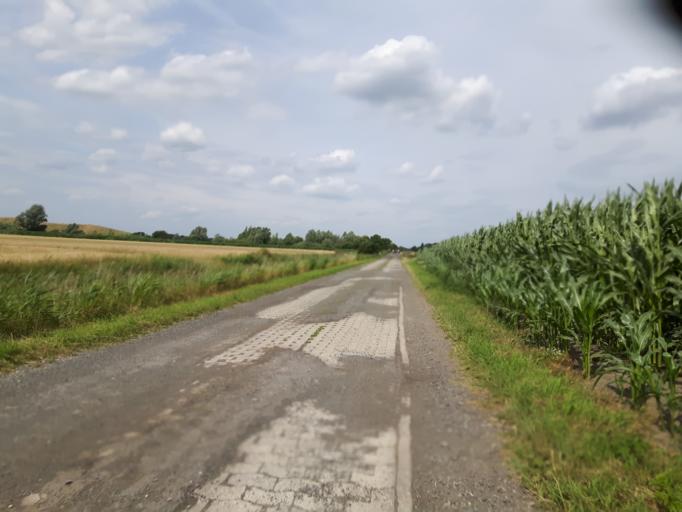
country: DE
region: Lower Saxony
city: Varel
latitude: 53.3959
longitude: 8.1904
